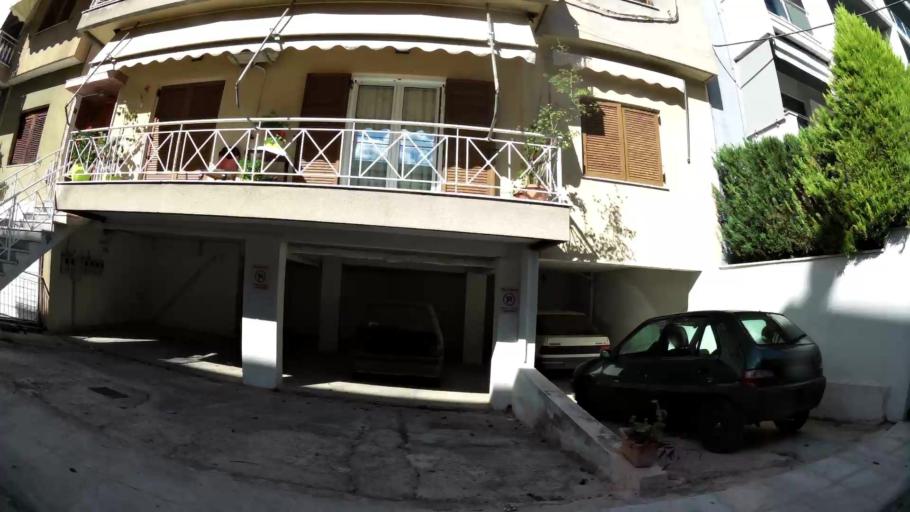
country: GR
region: Attica
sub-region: Nomarchia Athinas
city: Neo Psychiko
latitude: 38.0066
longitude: 23.7834
